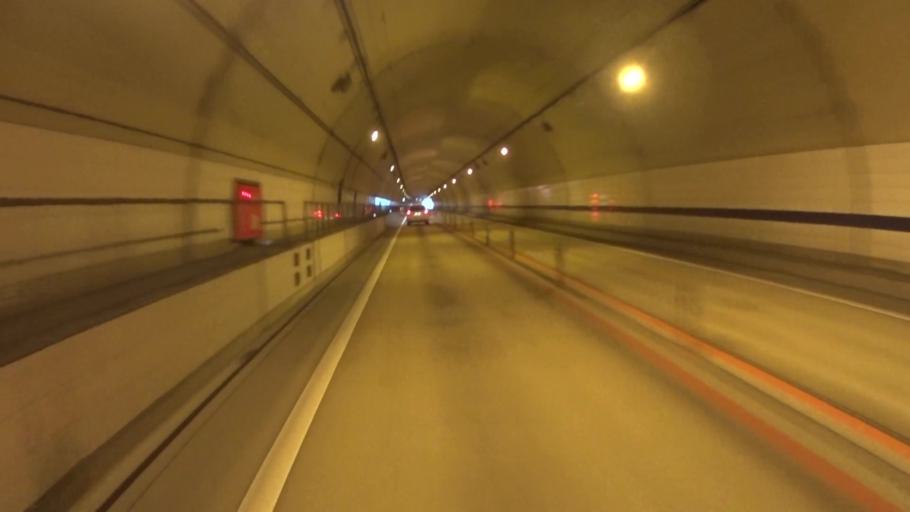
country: JP
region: Kyoto
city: Miyazu
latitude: 35.4772
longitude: 135.1748
